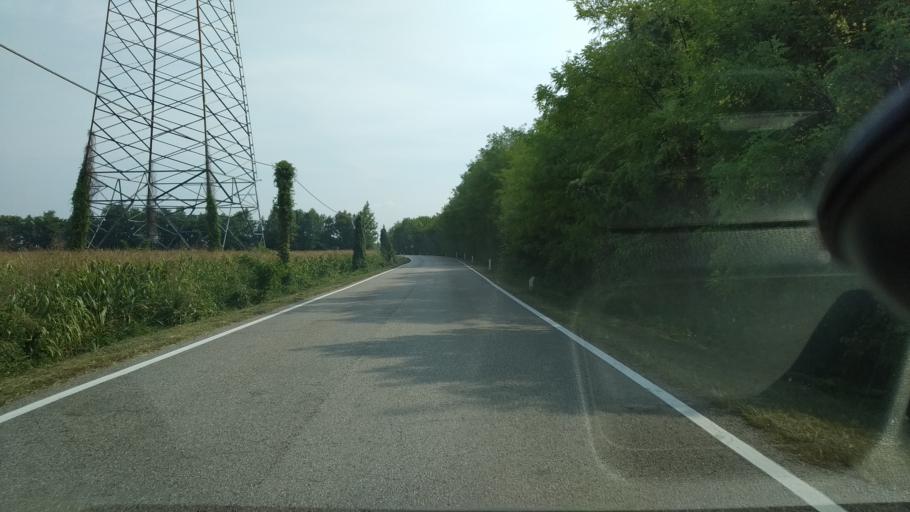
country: IT
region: Veneto
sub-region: Provincia di Vicenza
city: Tezze
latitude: 45.6695
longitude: 11.7112
